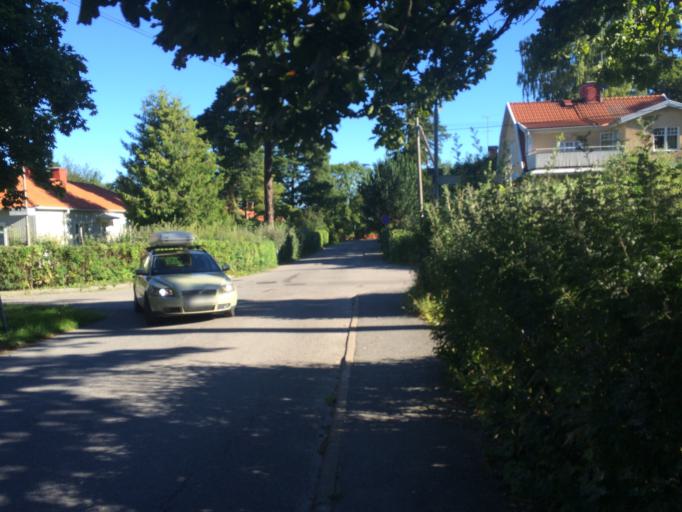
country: SE
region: Stockholm
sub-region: Stockholms Kommun
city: Kista
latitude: 59.3769
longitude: 17.8890
